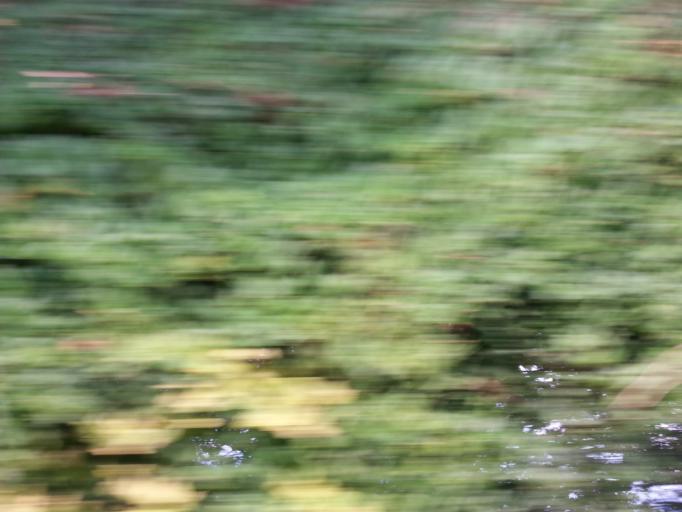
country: US
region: Tennessee
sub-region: Blount County
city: Wildwood
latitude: 35.8663
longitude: -83.8669
